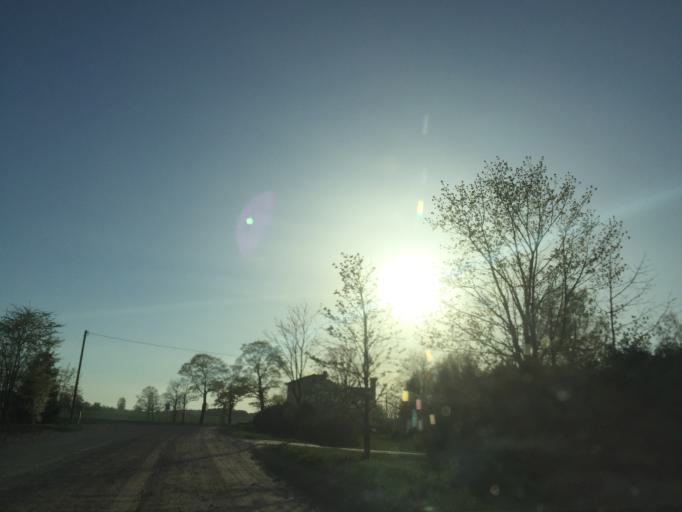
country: LV
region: Koknese
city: Koknese
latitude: 56.7320
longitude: 25.5485
